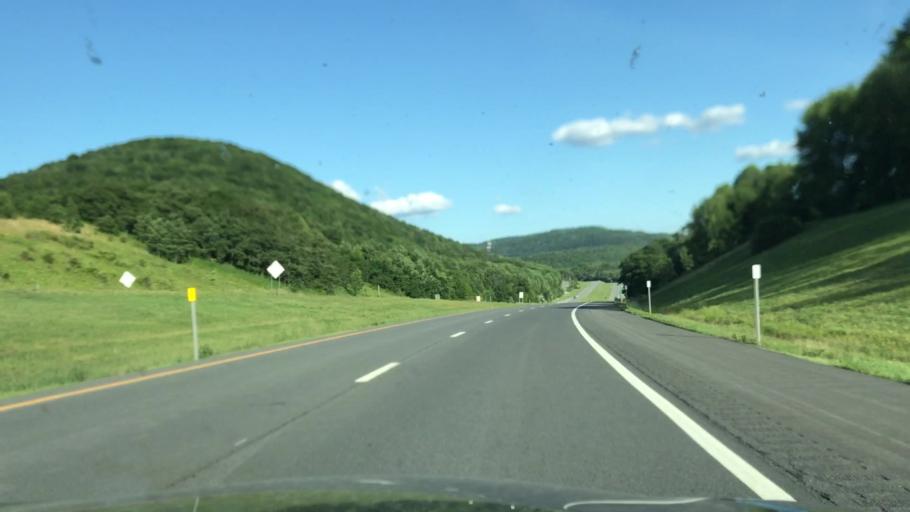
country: US
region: New York
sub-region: Sullivan County
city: Livingston Manor
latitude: 41.9614
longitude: -74.9946
